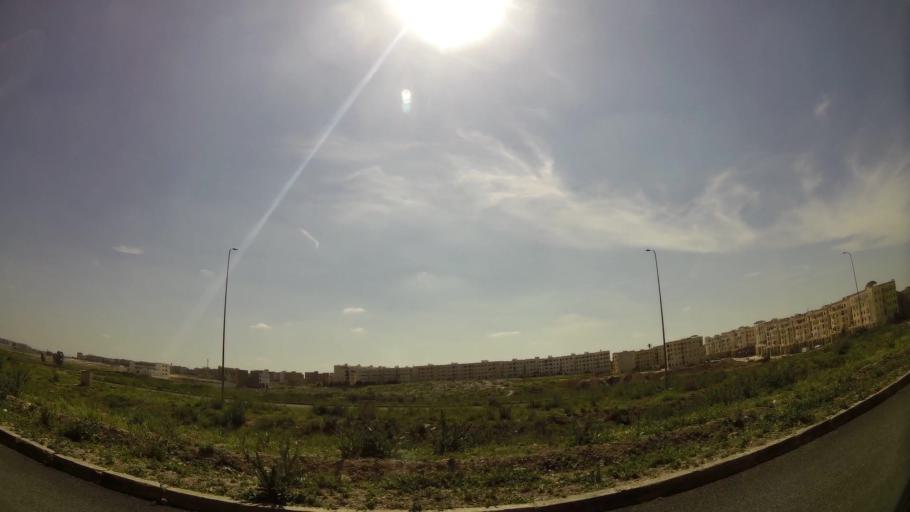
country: MA
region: Fes-Boulemane
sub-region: Fes
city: Fes
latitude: 34.0109
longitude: -5.0371
